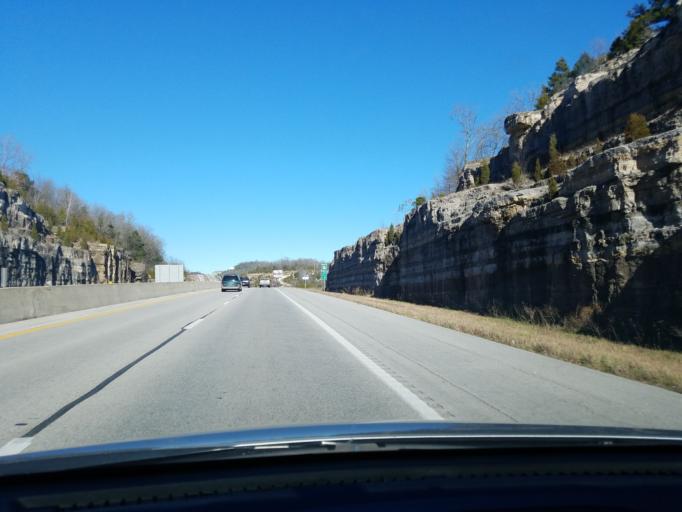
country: US
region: Missouri
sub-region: Taney County
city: Merriam Woods
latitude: 36.7295
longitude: -93.2206
